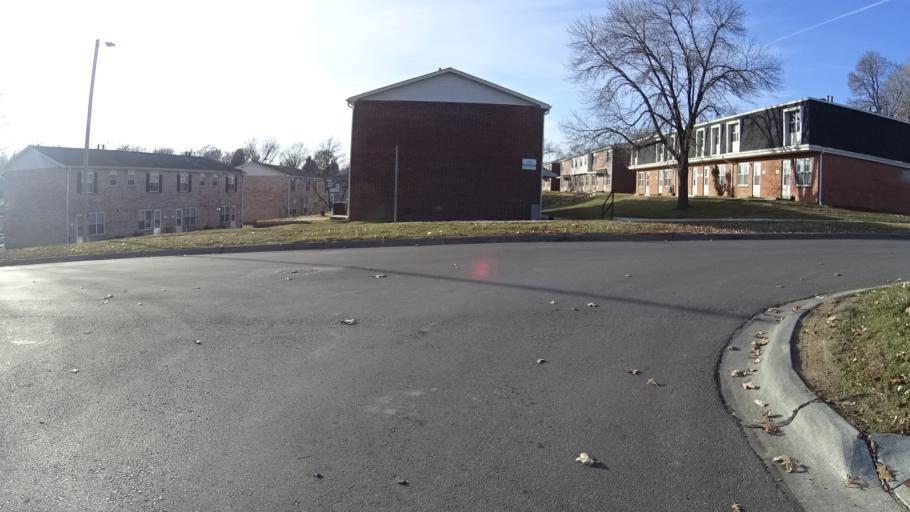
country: US
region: Nebraska
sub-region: Douglas County
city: Omaha
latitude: 41.1919
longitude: -95.9527
